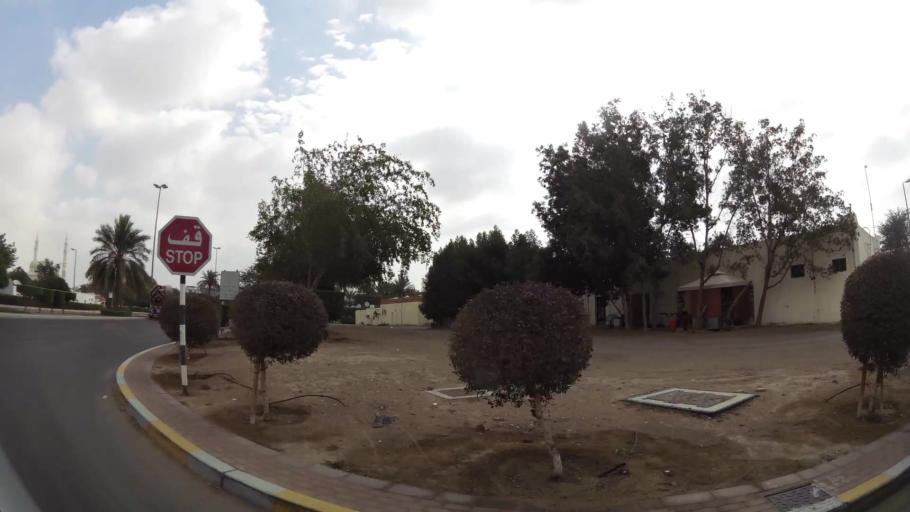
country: AE
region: Abu Dhabi
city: Al Ain
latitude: 24.2266
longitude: 55.7533
